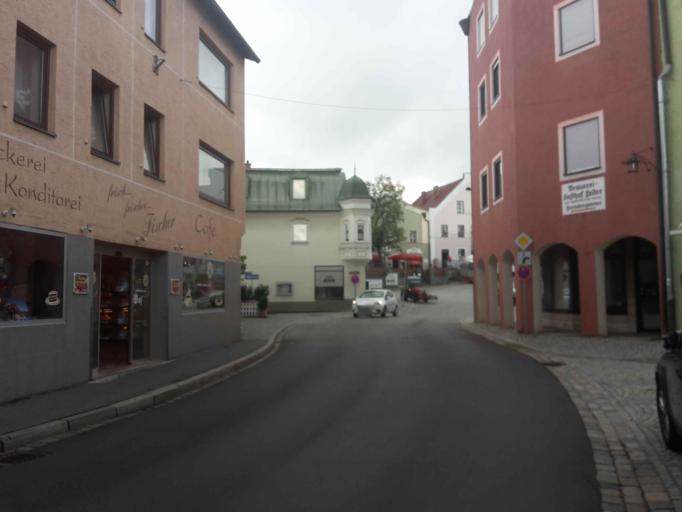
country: DE
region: Bavaria
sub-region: Lower Bavaria
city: Regen
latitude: 48.9696
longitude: 13.1273
